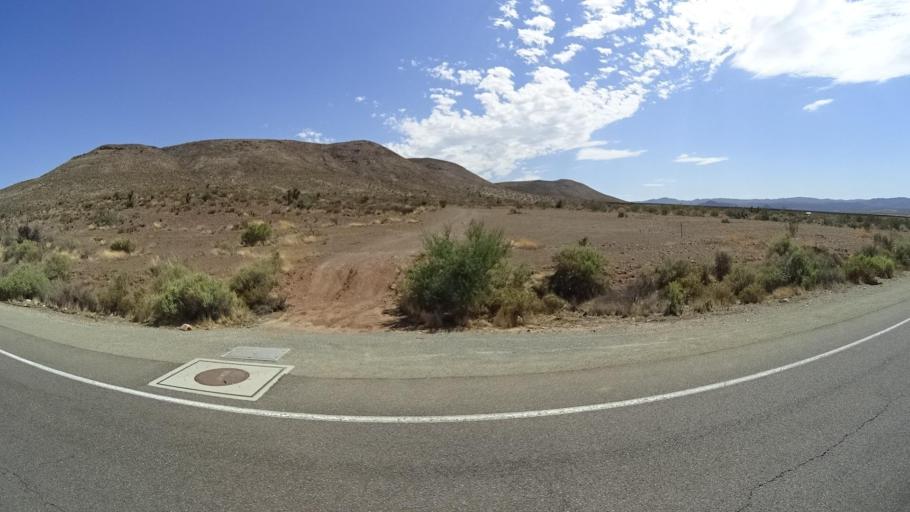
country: MX
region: Baja California
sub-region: Tecate
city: Cereso del Hongo
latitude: 32.6234
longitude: -116.1533
